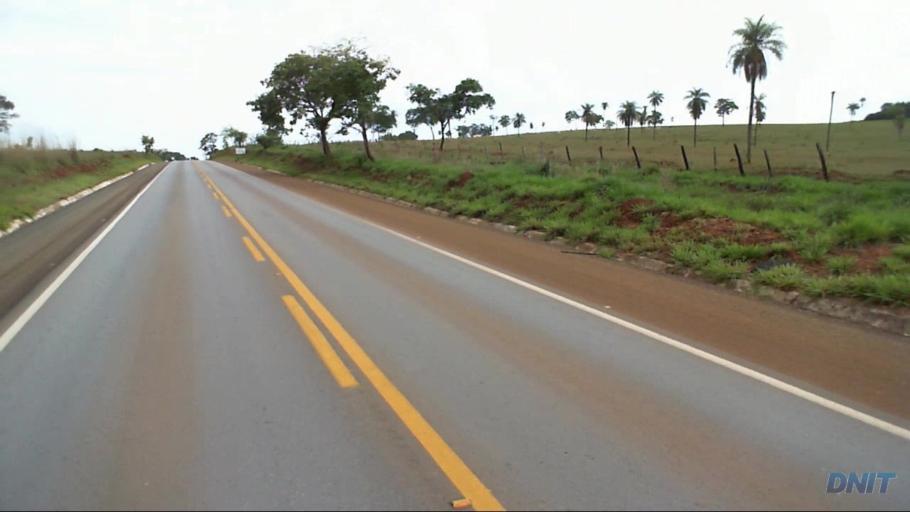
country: BR
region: Goias
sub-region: Uruacu
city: Uruacu
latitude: -14.6867
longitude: -49.1308
